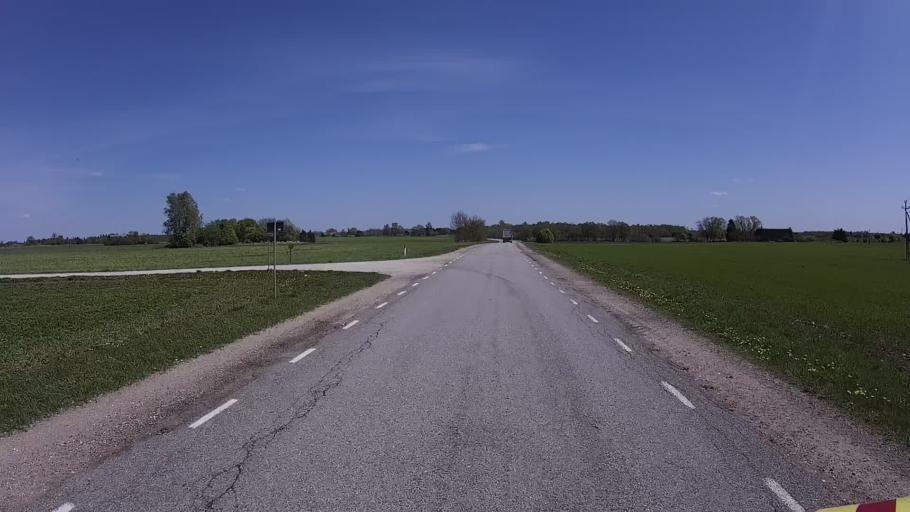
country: EE
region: Laeaene
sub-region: Ridala Parish
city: Uuemoisa
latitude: 59.0029
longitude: 23.7408
